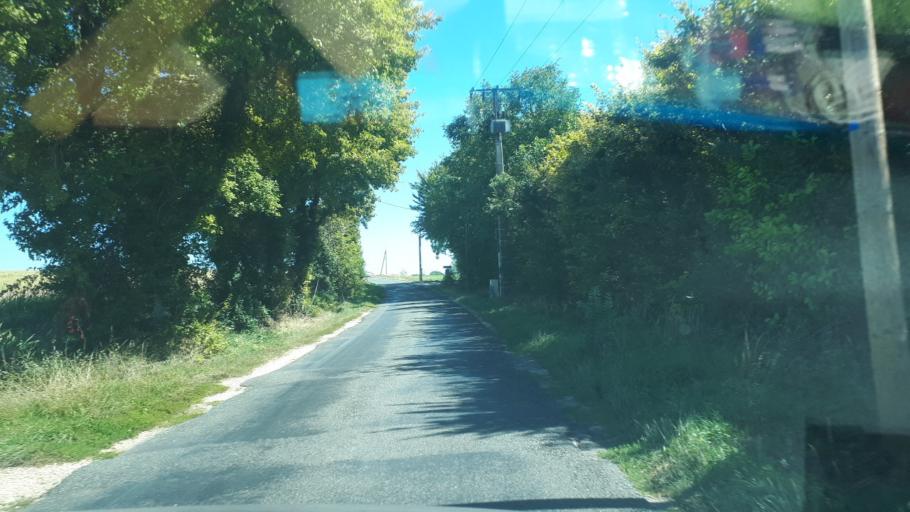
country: FR
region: Centre
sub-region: Departement du Cher
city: Rians
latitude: 47.1830
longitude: 2.5894
